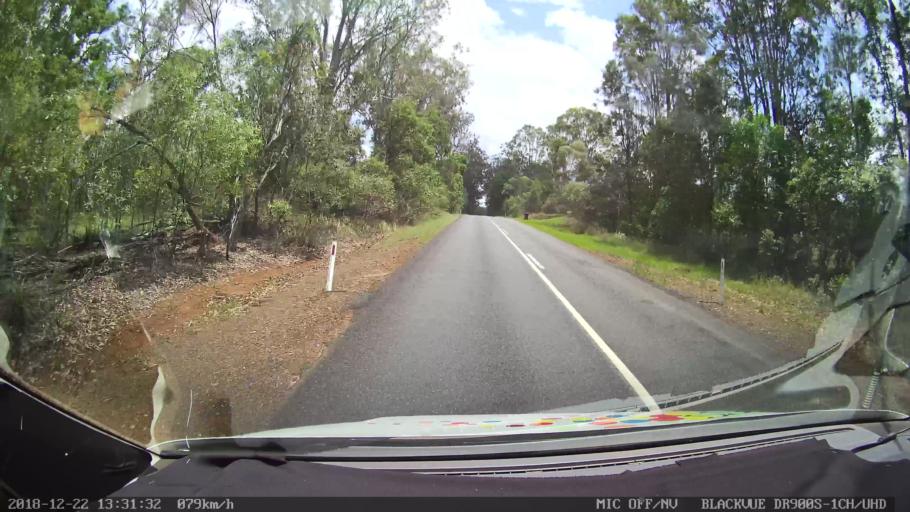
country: AU
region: New South Wales
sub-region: Clarence Valley
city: Coutts Crossing
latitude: -29.8564
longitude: 152.8519
